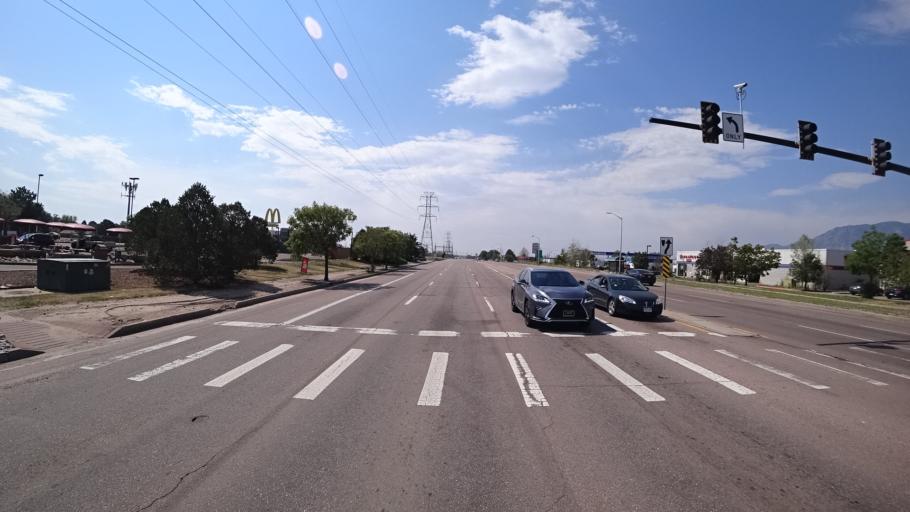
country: US
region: Colorado
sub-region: El Paso County
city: Stratmoor
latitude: 38.7963
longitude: -104.7575
